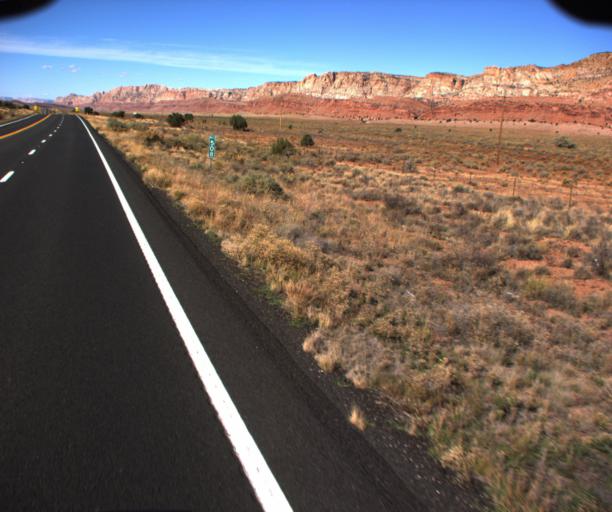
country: US
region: Arizona
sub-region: Coconino County
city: Tuba City
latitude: 36.4274
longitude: -111.5469
